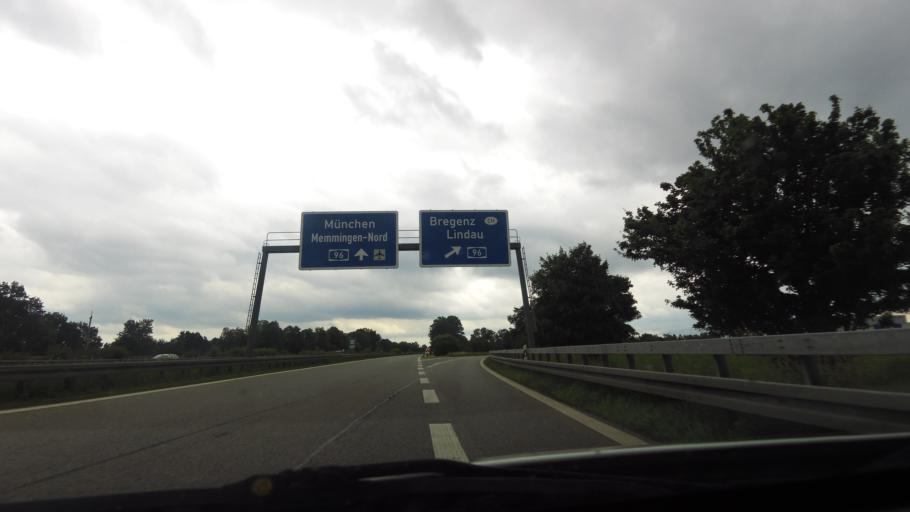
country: DE
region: Bavaria
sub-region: Swabia
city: Buxheim
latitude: 48.0005
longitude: 10.1494
